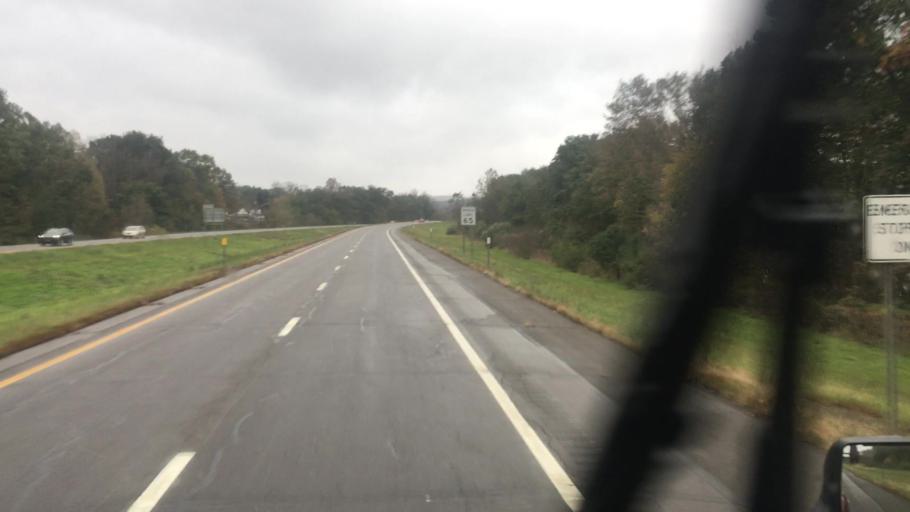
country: US
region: New York
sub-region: Tioga County
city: Apalachin
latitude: 42.0742
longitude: -76.1537
